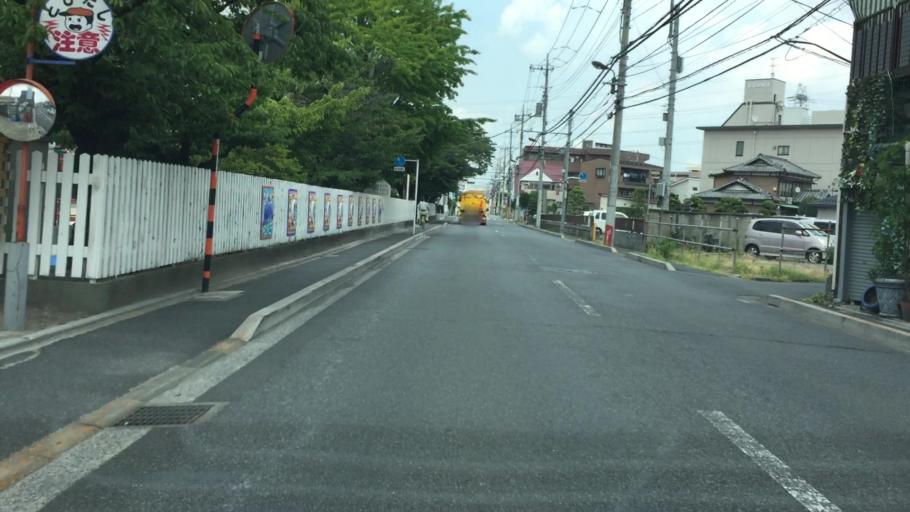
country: JP
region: Saitama
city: Soka
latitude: 35.7759
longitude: 139.8165
